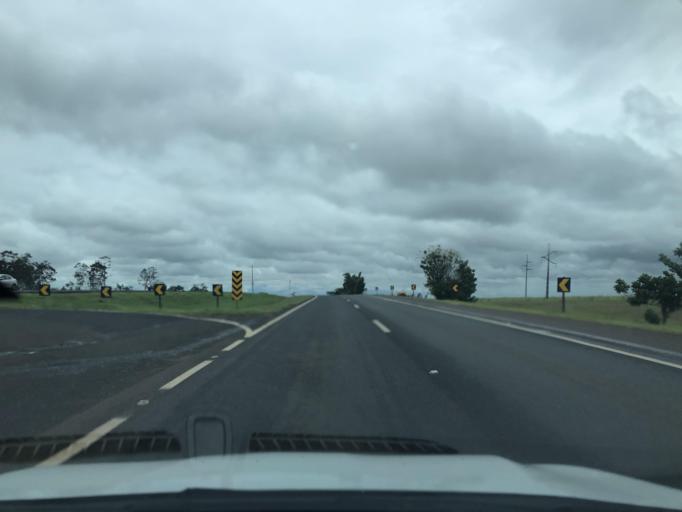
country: BR
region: Minas Gerais
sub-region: Uberaba
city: Uberaba
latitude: -19.6371
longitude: -48.0114
